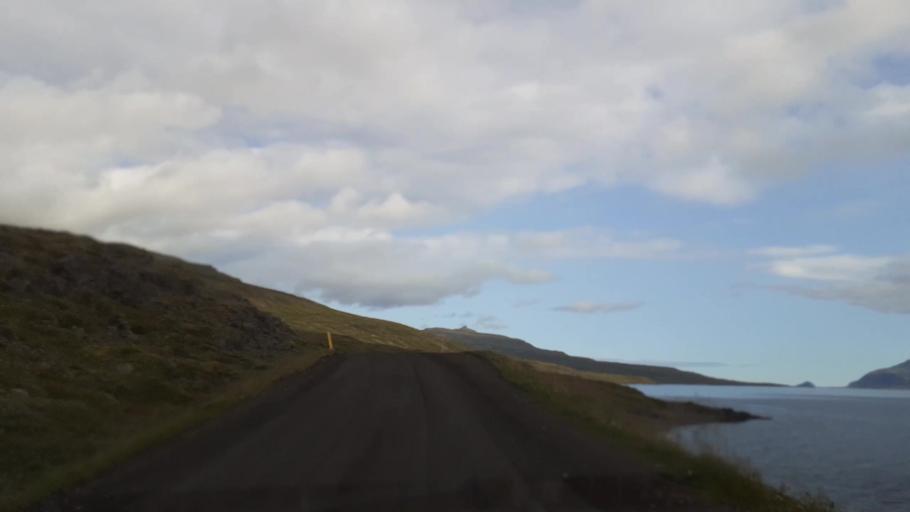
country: IS
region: East
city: Eskifjoerdur
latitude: 65.0406
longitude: -13.8909
